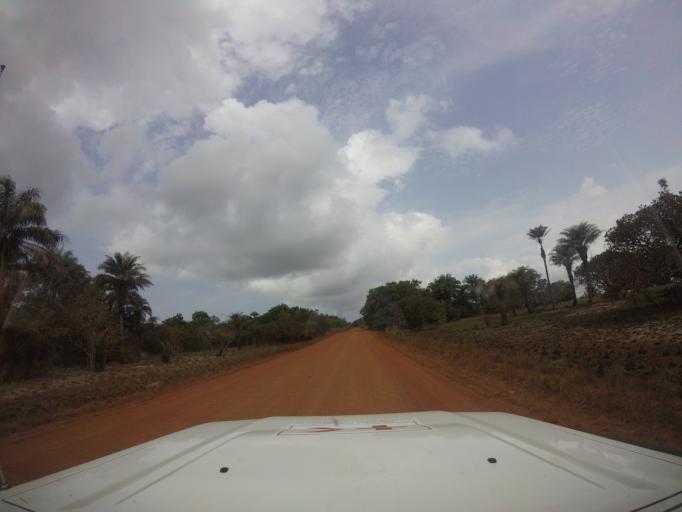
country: LR
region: Grand Cape Mount
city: Robertsport
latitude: 6.6896
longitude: -11.2585
